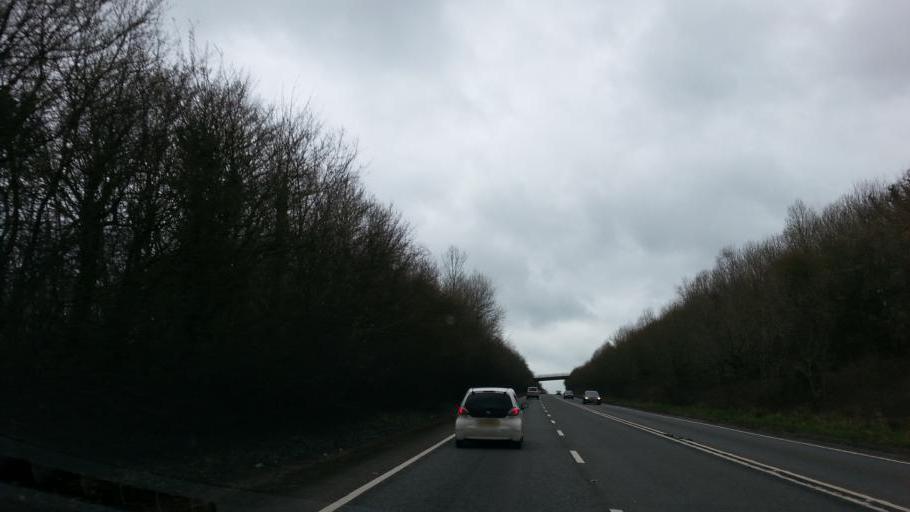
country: GB
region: England
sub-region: Devon
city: South Molton
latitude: 51.0187
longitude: -3.7972
